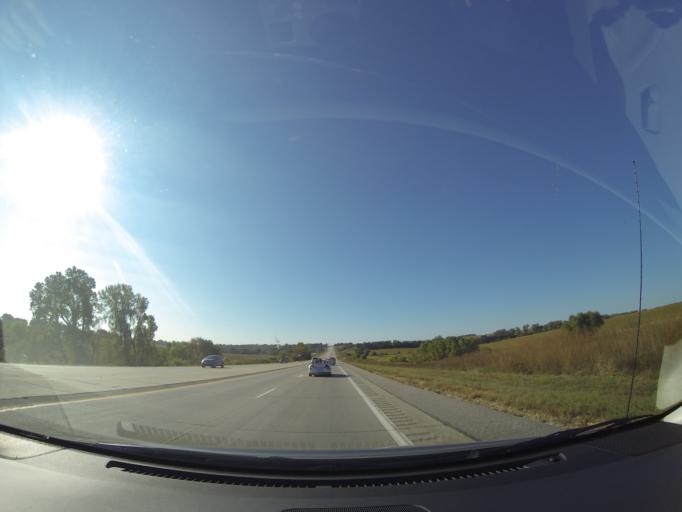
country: US
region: Nebraska
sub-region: Sarpy County
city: Gretna
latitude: 41.1799
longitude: -96.2344
